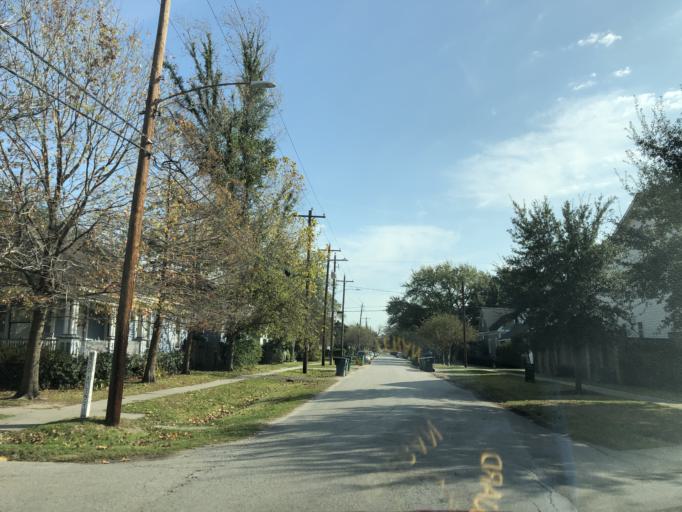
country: US
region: Texas
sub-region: Harris County
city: Houston
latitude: 29.7926
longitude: -95.3944
